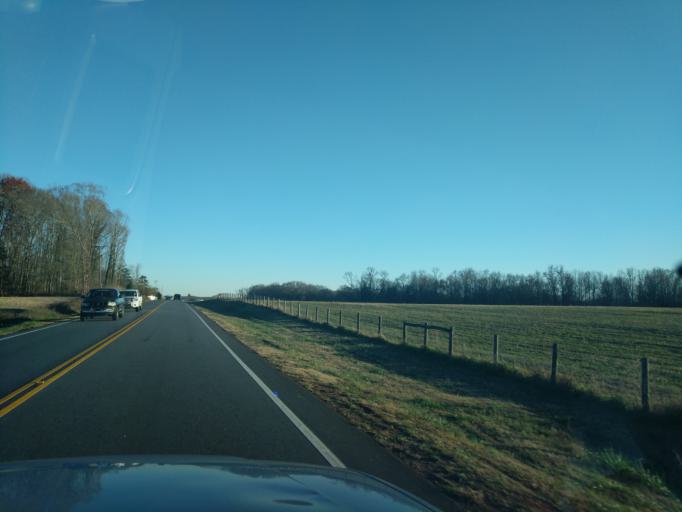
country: US
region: South Carolina
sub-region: Oconee County
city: Utica
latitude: 34.5882
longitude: -82.9509
